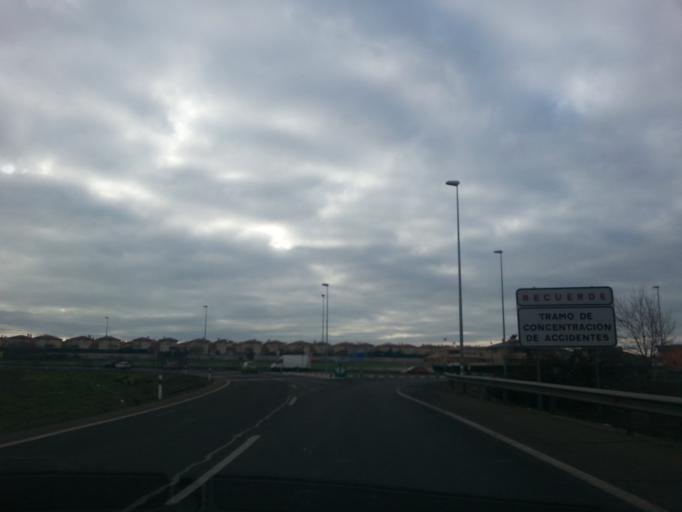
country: ES
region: Castille and Leon
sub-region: Provincia de Salamanca
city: Carbajosa de la Sagrada
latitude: 40.9433
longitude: -5.6418
